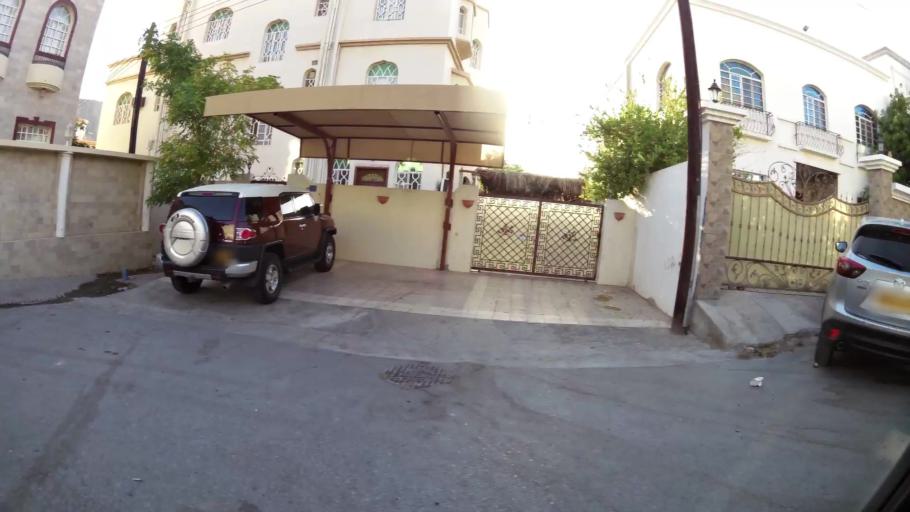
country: OM
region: Muhafazat Masqat
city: Muscat
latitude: 23.5660
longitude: 58.5822
